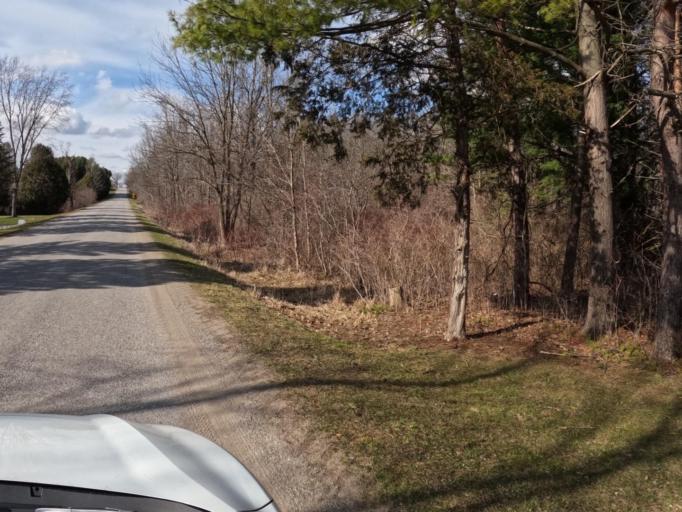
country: CA
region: Ontario
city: Norfolk County
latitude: 42.8919
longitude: -80.2860
